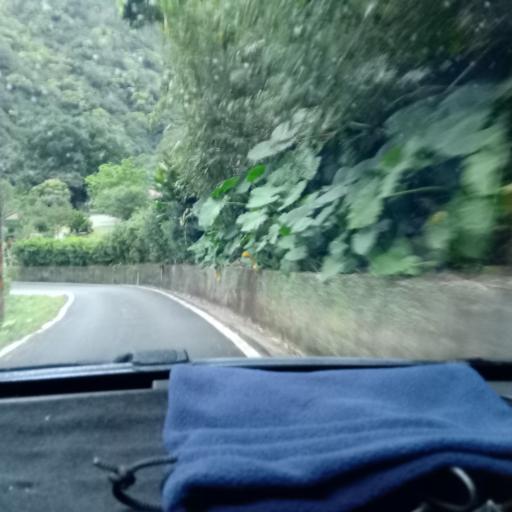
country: TW
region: Taiwan
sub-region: Yilan
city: Yilan
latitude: 24.8072
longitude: 121.7008
